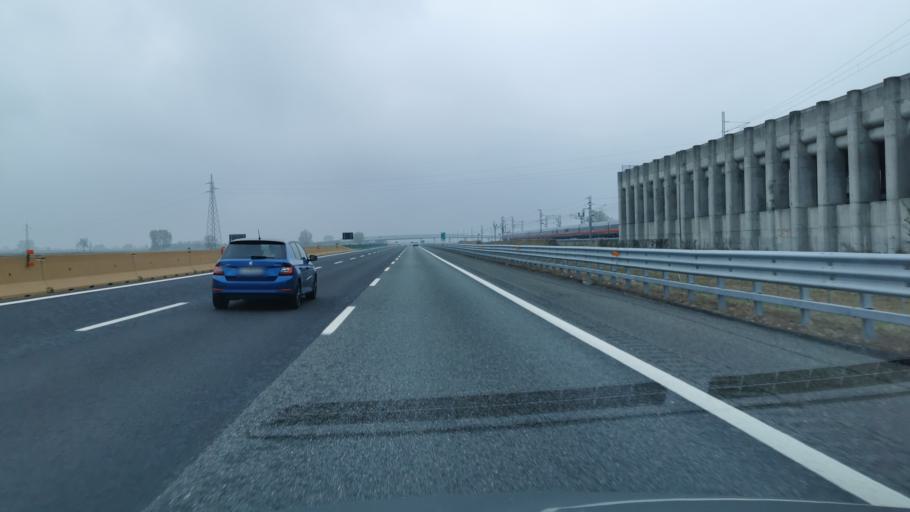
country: IT
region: Piedmont
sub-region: Provincia di Vercelli
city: Cigliano
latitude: 45.3018
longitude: 8.0518
